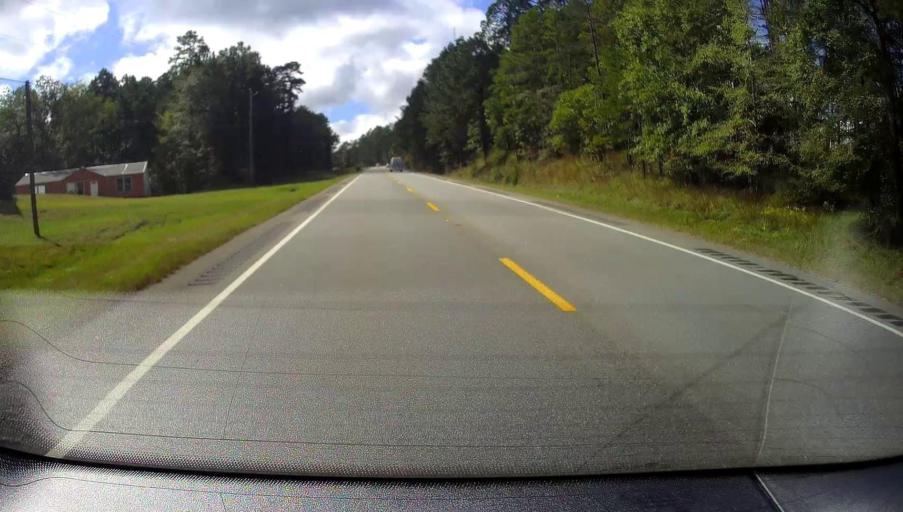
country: US
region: Georgia
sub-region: Baldwin County
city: Milledgeville
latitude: 33.0681
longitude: -83.2675
